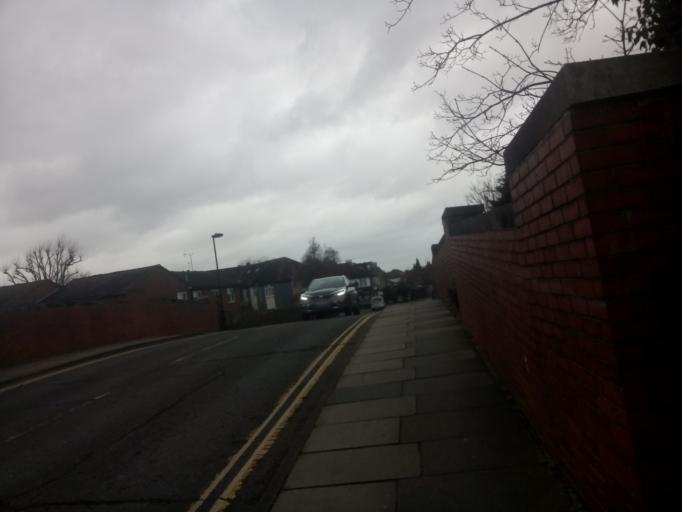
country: GB
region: England
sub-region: Greater London
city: Hampton
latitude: 51.4163
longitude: -0.3697
